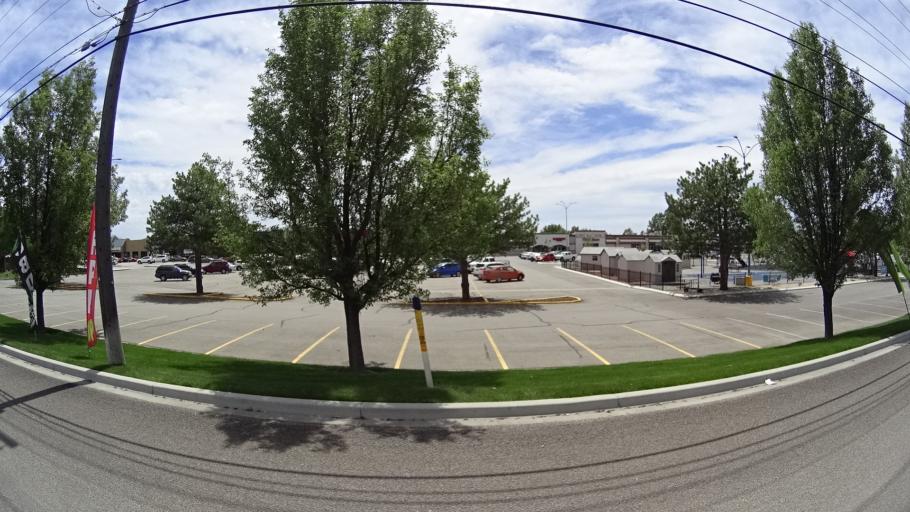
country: US
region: Idaho
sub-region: Ada County
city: Garden City
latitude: 43.6194
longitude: -116.3120
